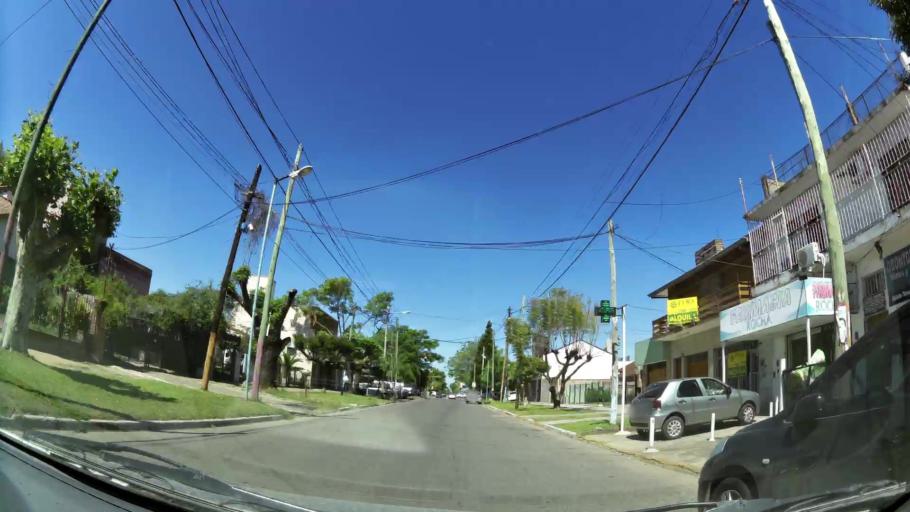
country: AR
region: Buenos Aires
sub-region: Partido de Quilmes
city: Quilmes
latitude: -34.7156
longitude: -58.3039
